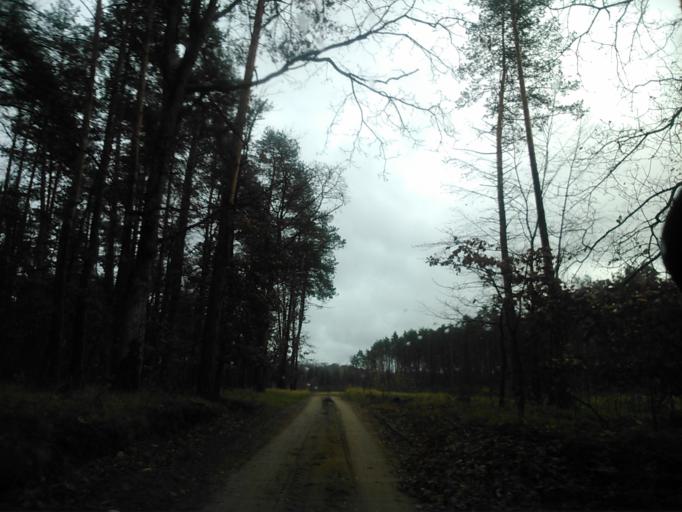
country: PL
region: Kujawsko-Pomorskie
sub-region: Powiat golubsko-dobrzynski
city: Radomin
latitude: 53.1387
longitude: 19.1458
